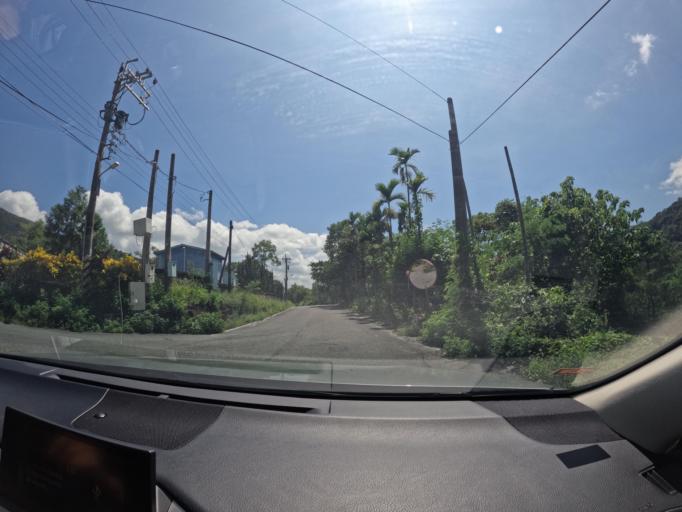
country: TW
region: Taiwan
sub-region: Hualien
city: Hualian
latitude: 23.5873
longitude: 121.3573
